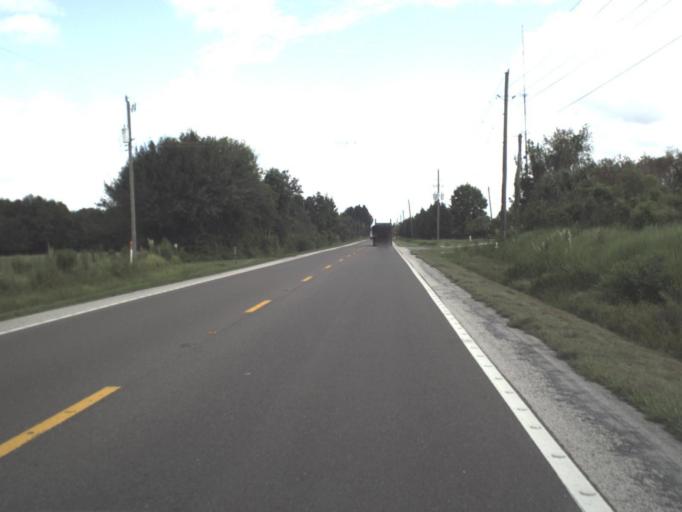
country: US
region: Florida
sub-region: Hardee County
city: Zolfo Springs
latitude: 27.3613
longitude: -81.7998
